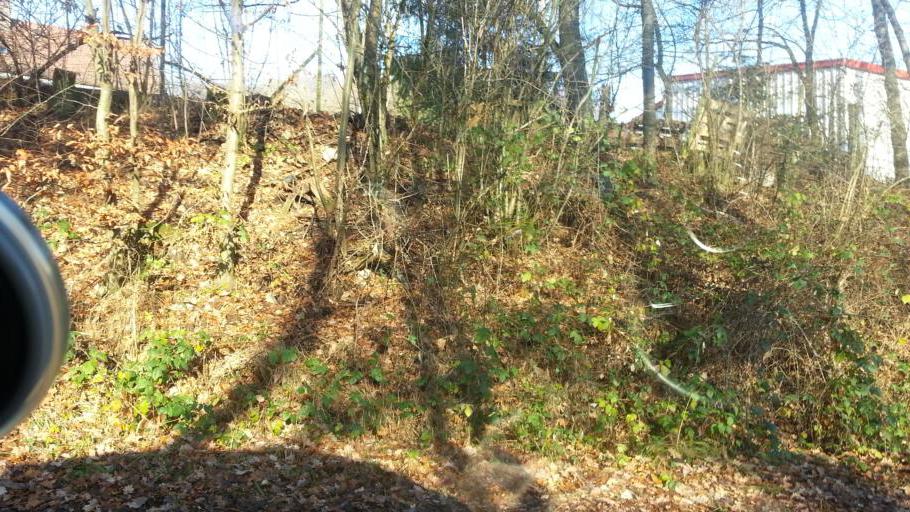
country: DE
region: Saarland
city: Tholey
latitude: 49.4833
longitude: 7.0412
